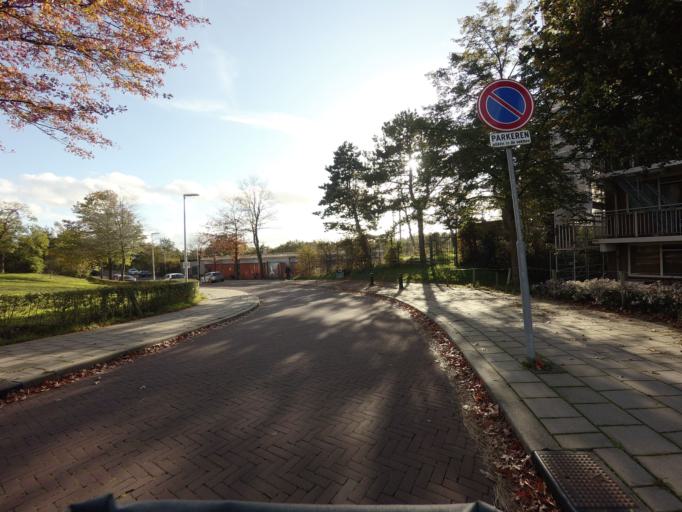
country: NL
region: North Holland
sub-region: Gemeente Bussum
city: Bussum
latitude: 52.2617
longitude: 5.1691
